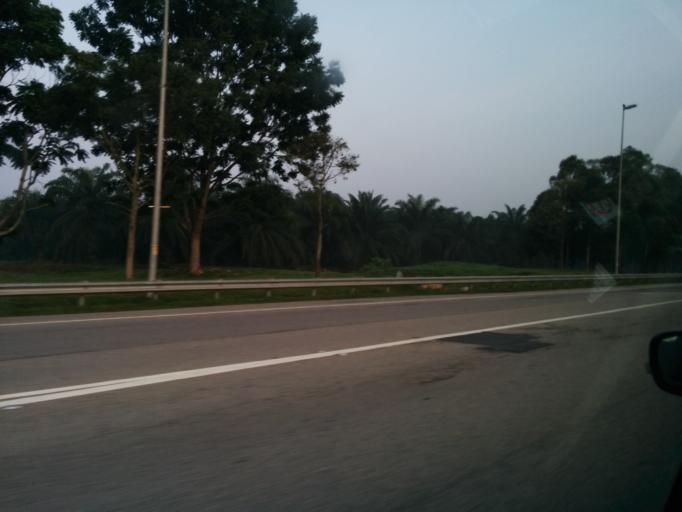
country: MY
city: Sungai Pelek New Village
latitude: 2.7555
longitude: 101.6884
